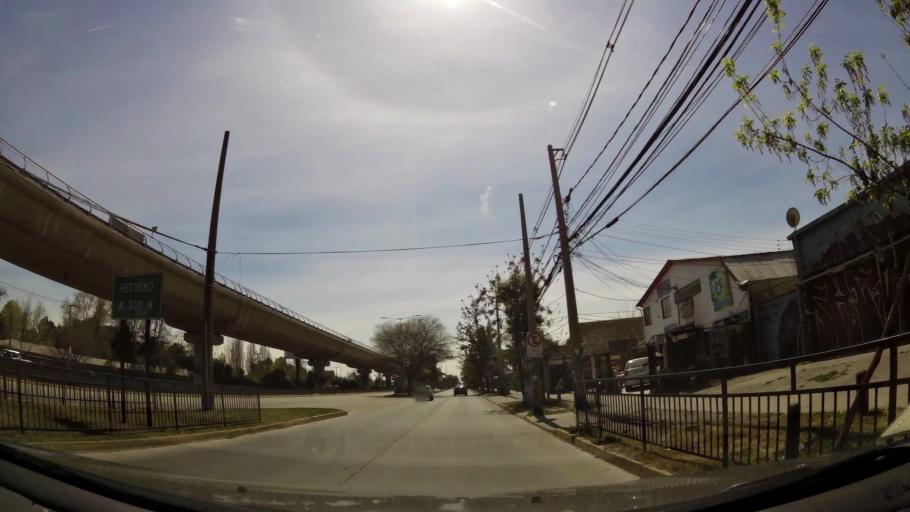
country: CL
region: Santiago Metropolitan
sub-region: Provincia de Cordillera
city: Puente Alto
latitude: -33.5940
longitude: -70.5788
